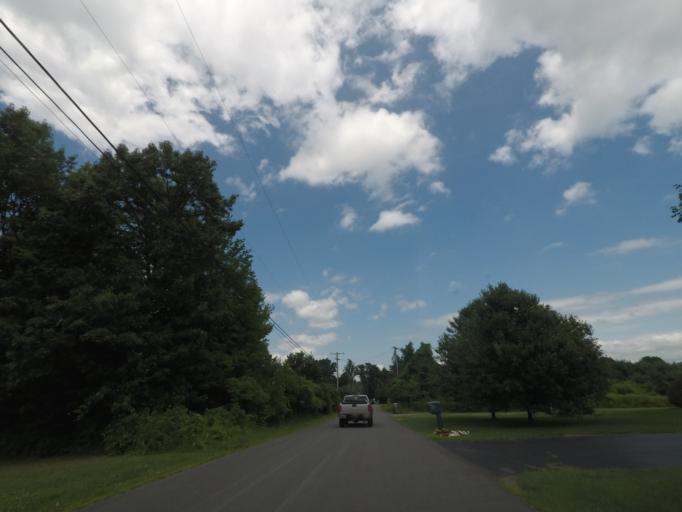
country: US
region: New York
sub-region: Rensselaer County
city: East Greenbush
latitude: 42.5306
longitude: -73.6903
